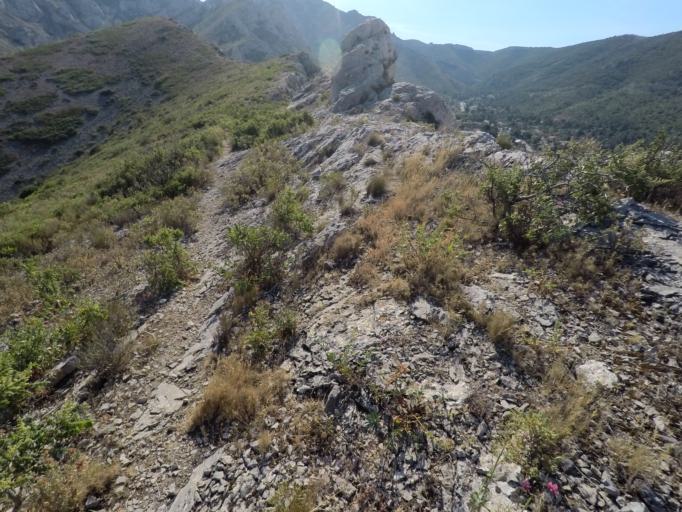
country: FR
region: Provence-Alpes-Cote d'Azur
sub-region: Departement des Bouches-du-Rhone
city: Marseille 09
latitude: 43.2527
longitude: 5.4396
